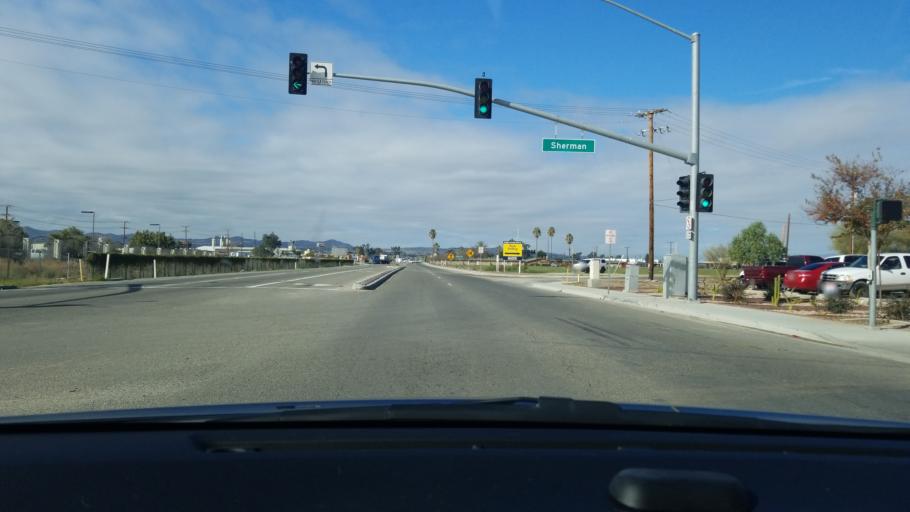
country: US
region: California
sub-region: Riverside County
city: Romoland
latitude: 33.7487
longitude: -117.1800
